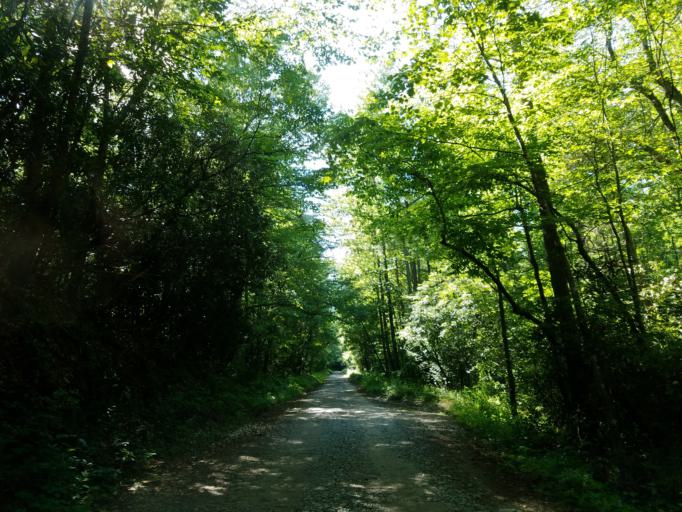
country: US
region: Georgia
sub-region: Dawson County
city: Dawsonville
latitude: 34.5817
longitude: -84.1828
